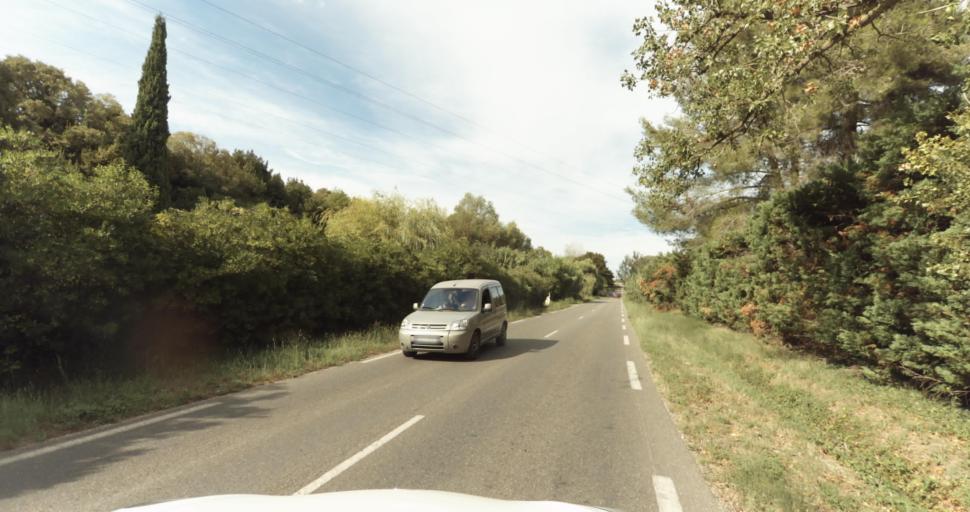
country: FR
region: Provence-Alpes-Cote d'Azur
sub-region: Departement des Bouches-du-Rhone
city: Miramas
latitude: 43.5675
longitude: 5.0156
